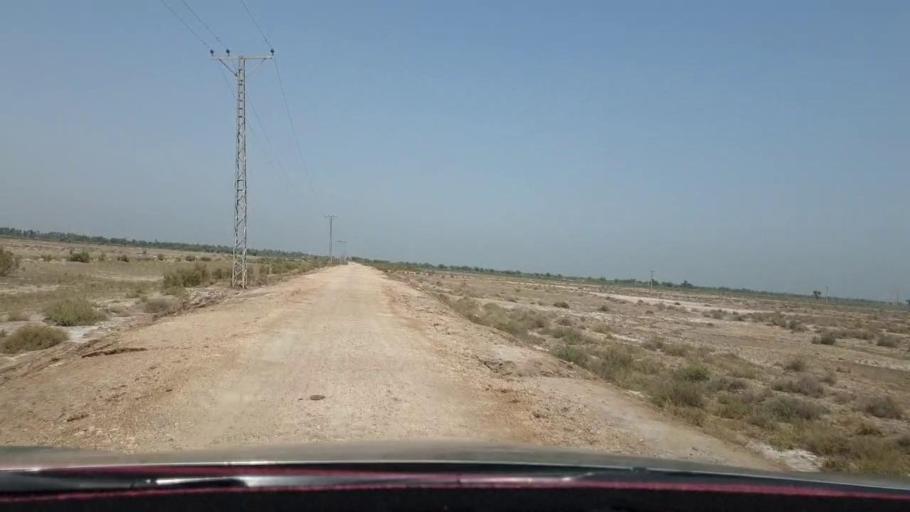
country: PK
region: Sindh
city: Warah
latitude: 27.3935
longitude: 67.6848
